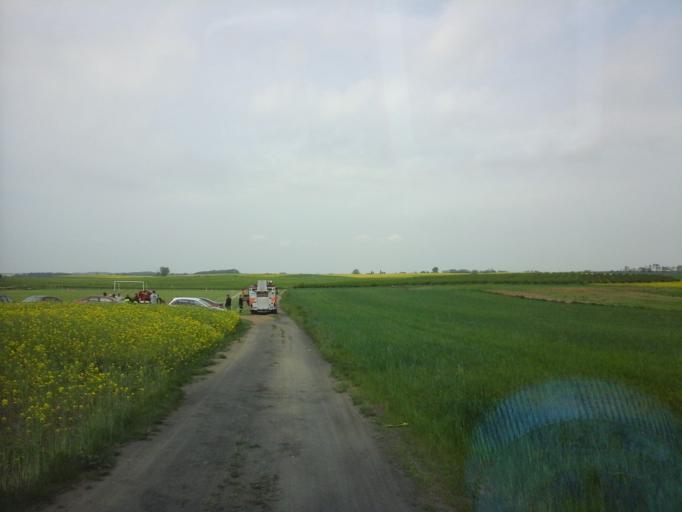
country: PL
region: West Pomeranian Voivodeship
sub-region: Powiat choszczenski
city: Pelczyce
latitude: 53.0167
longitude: 15.3703
